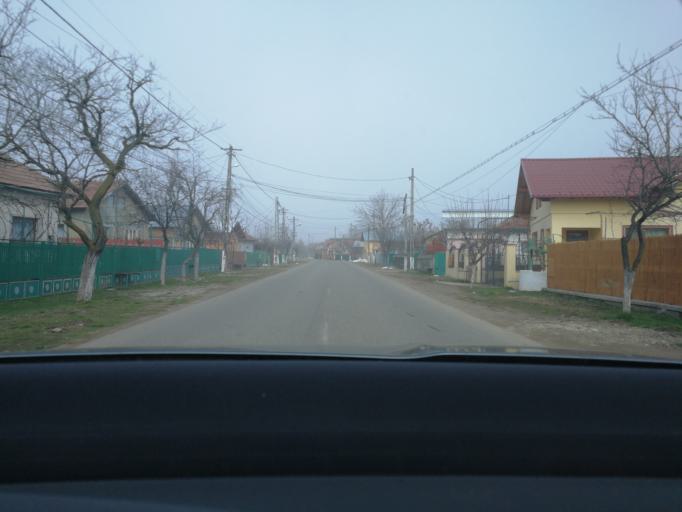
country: RO
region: Prahova
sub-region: Comuna Magureni
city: Lunca Prahovei
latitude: 45.0386
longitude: 25.7574
